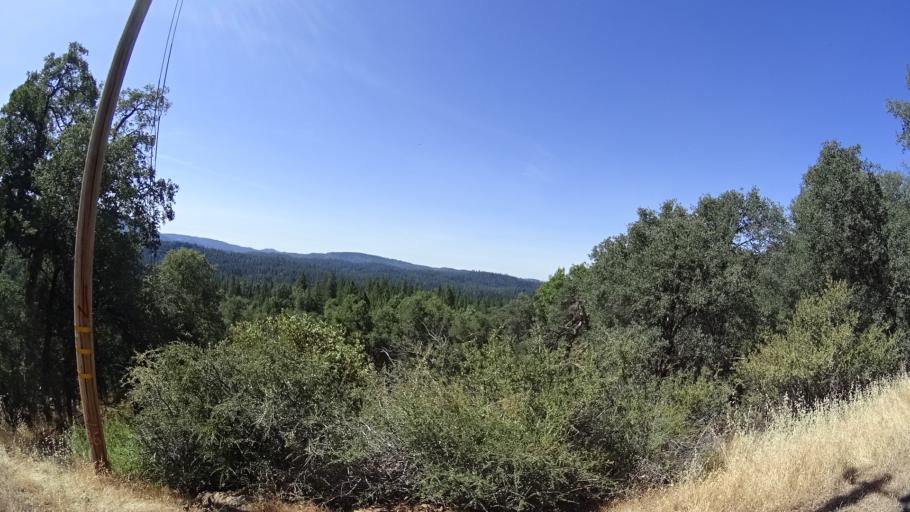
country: US
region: California
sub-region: Amador County
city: Pioneer
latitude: 38.4030
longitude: -120.4573
